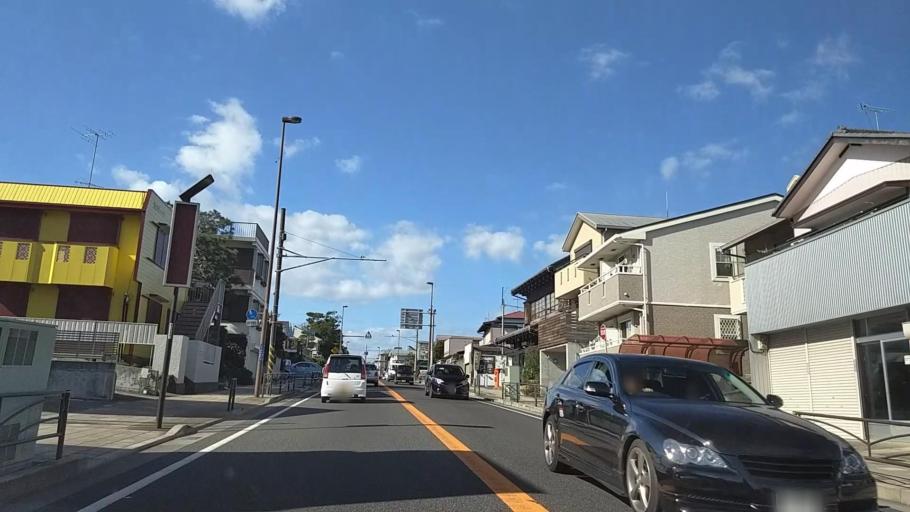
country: JP
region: Kanagawa
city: Oiso
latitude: 35.3078
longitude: 139.3104
